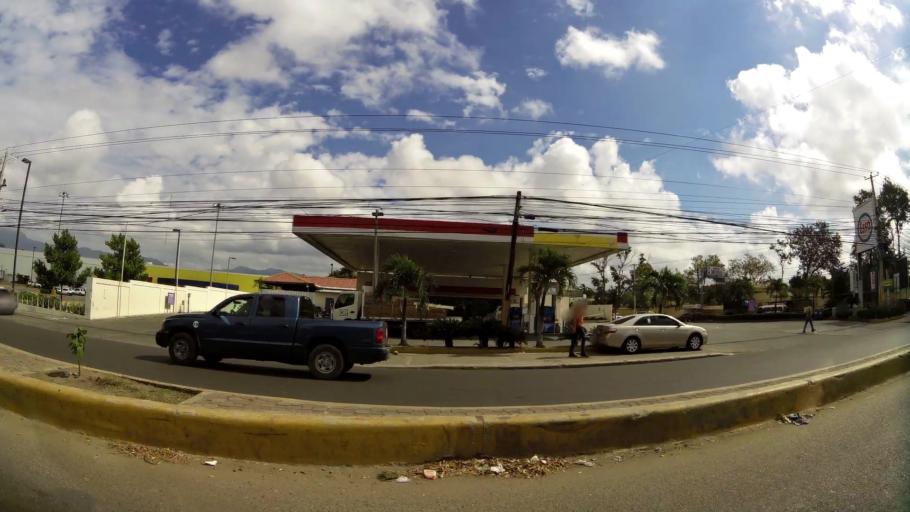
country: DO
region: Santiago
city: Santiago de los Caballeros
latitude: 19.4832
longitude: -70.7092
